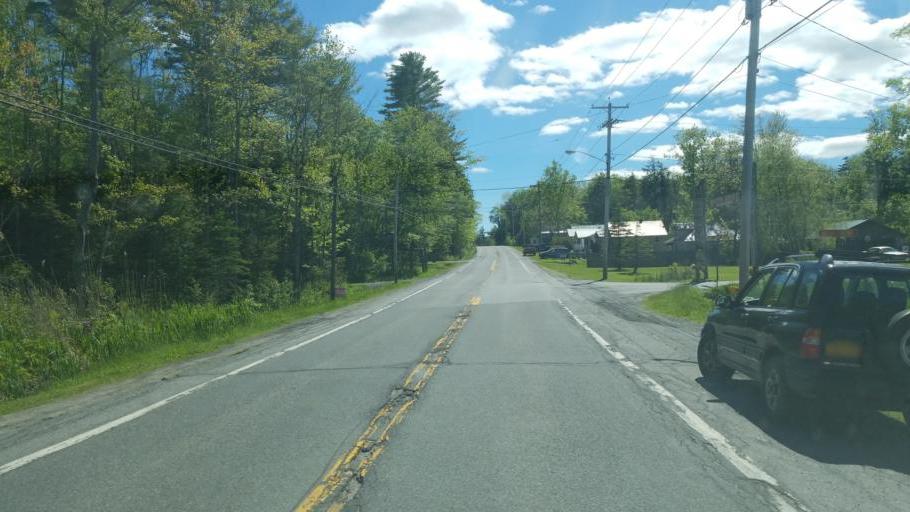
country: US
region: New York
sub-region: Fulton County
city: Gloversville
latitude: 43.1305
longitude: -74.4918
